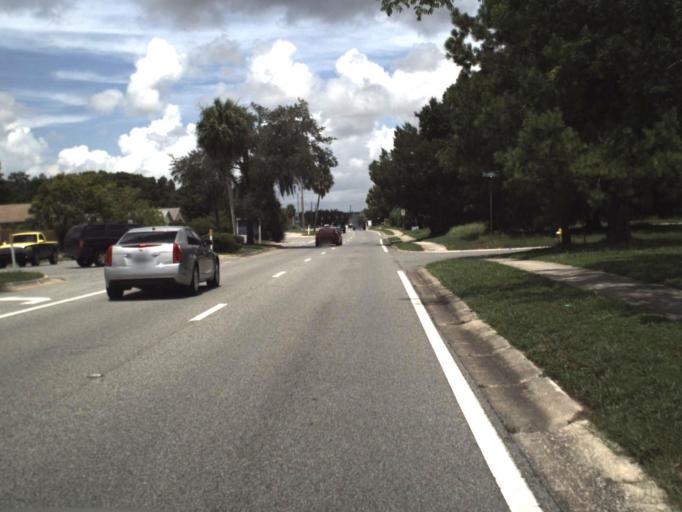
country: US
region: Florida
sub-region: Pasco County
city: Elfers
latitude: 28.2134
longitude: -82.6926
